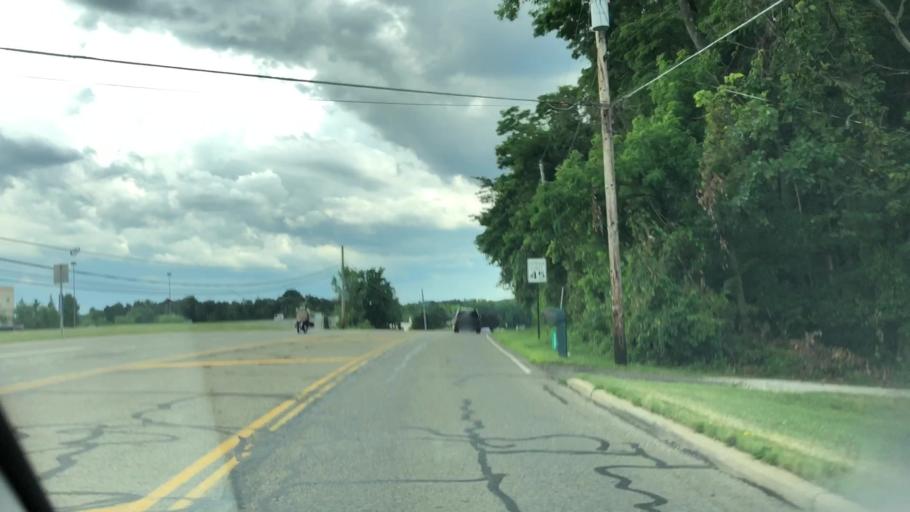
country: US
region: Ohio
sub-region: Summit County
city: Greensburg
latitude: 40.9135
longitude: -81.4619
